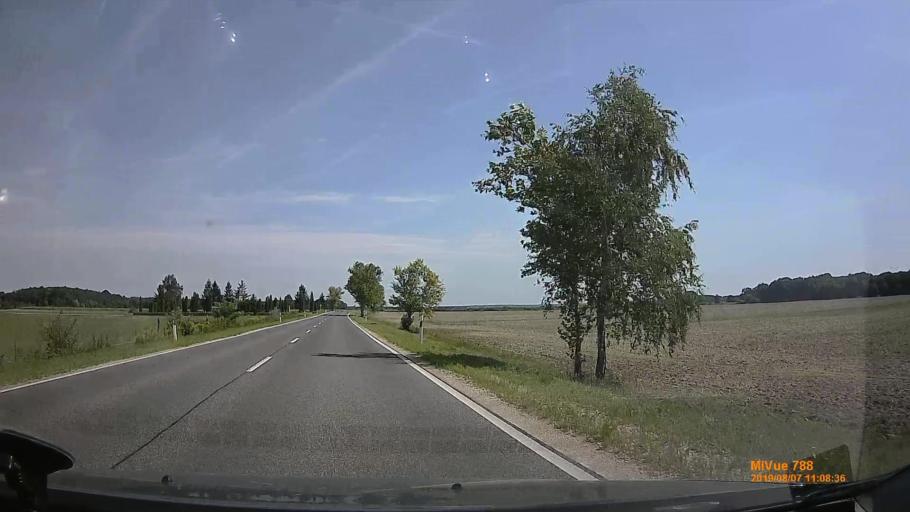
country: HU
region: Zala
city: Lenti
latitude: 46.6385
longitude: 16.4825
